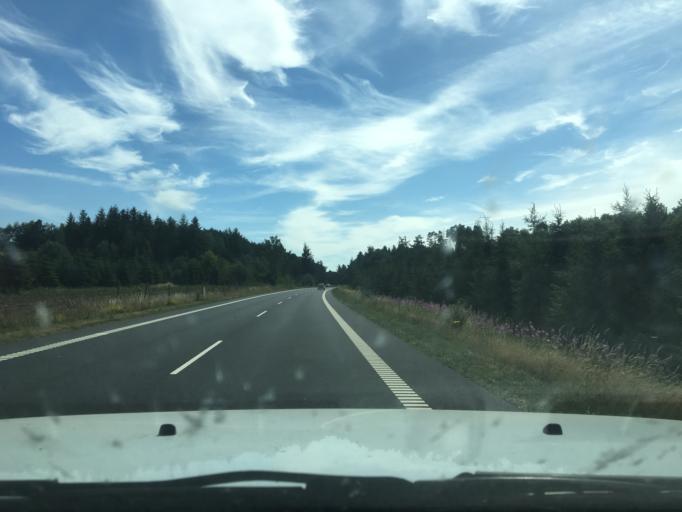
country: DK
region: Central Jutland
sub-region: Viborg Kommune
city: Viborg
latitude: 56.5167
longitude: 9.4029
